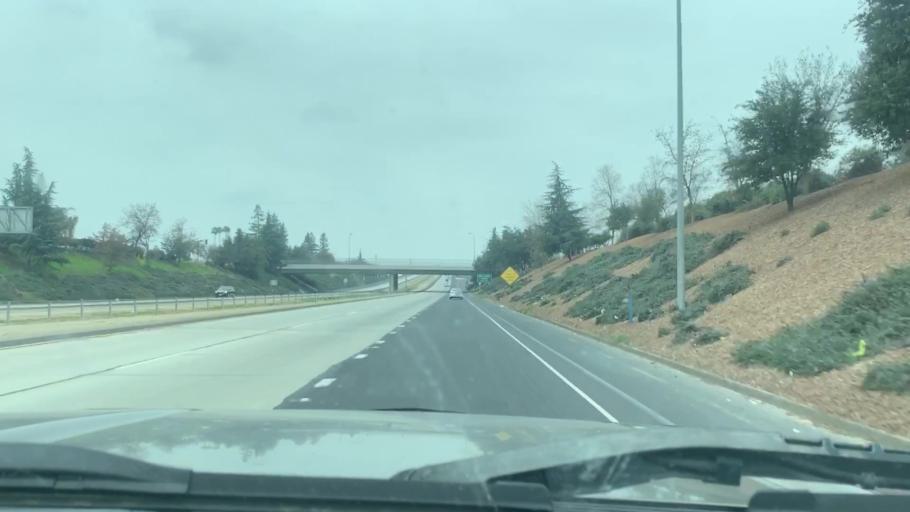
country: US
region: California
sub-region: Tulare County
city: Visalia
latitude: 36.3276
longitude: -119.3384
